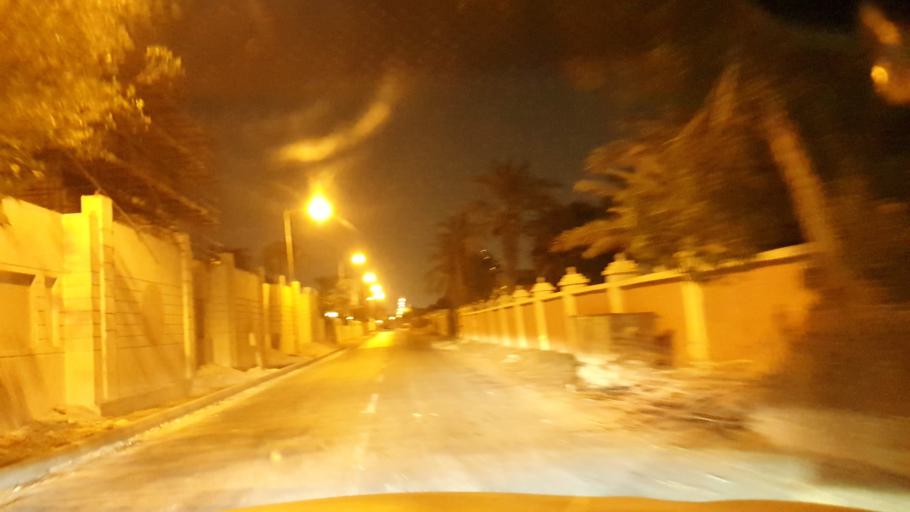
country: BH
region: Manama
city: Jidd Hafs
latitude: 26.1972
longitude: 50.4951
